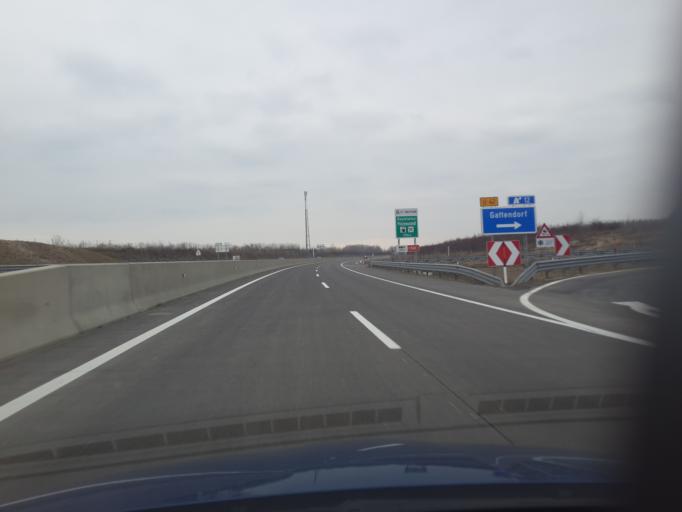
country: AT
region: Burgenland
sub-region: Politischer Bezirk Neusiedl am See
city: Gattendorf
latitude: 48.0365
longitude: 16.9843
